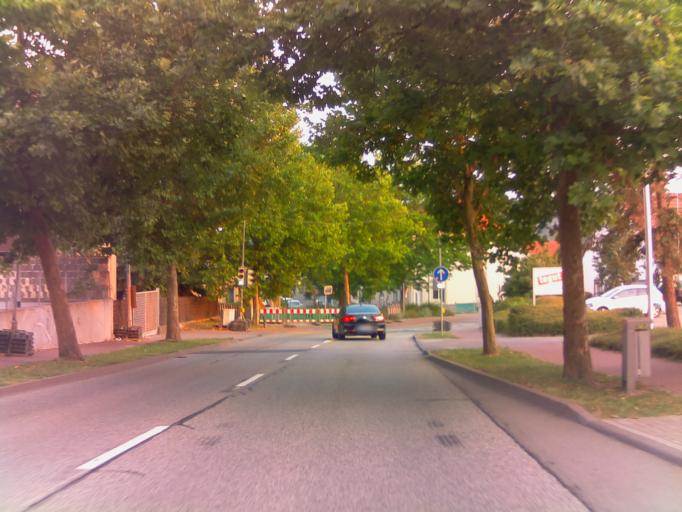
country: DE
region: Thuringia
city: Bad Berka
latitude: 50.9027
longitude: 11.2800
